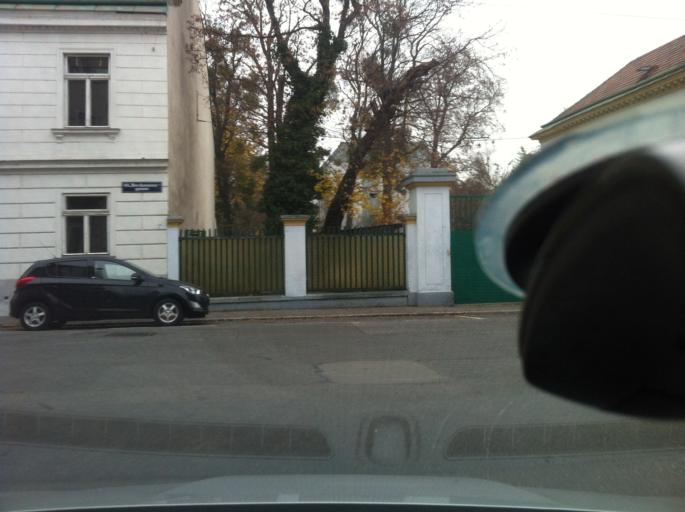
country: AT
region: Vienna
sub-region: Wien Stadt
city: Vienna
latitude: 48.1916
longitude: 16.3118
